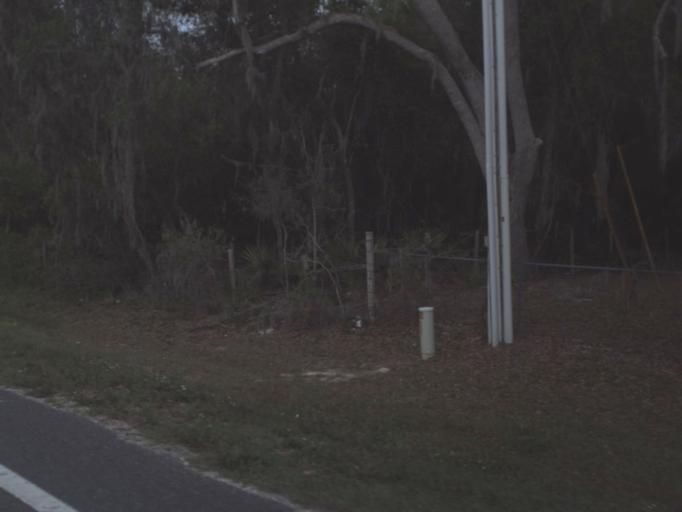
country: US
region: Florida
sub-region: Lake County
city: Groveland
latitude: 28.6212
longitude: -81.8258
